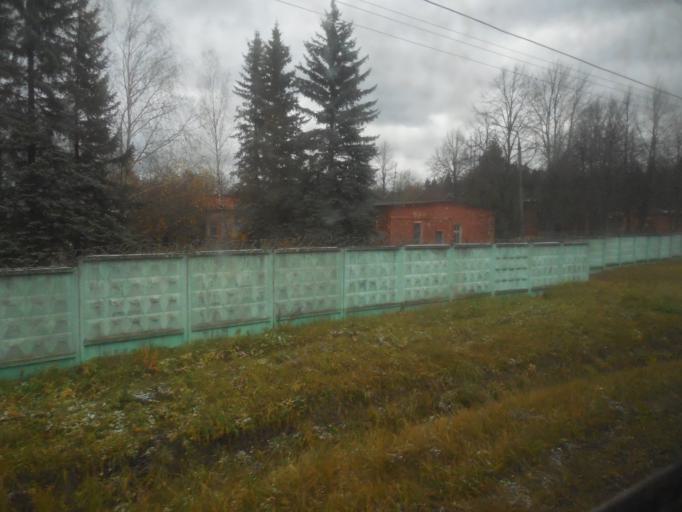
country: RU
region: Moskovskaya
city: Zvenigorod
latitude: 55.6959
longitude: 36.8712
